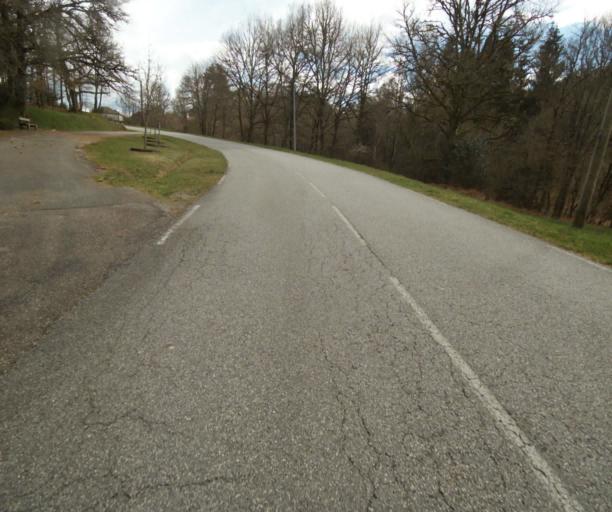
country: FR
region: Limousin
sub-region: Departement de la Correze
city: Correze
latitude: 45.3365
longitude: 1.9367
